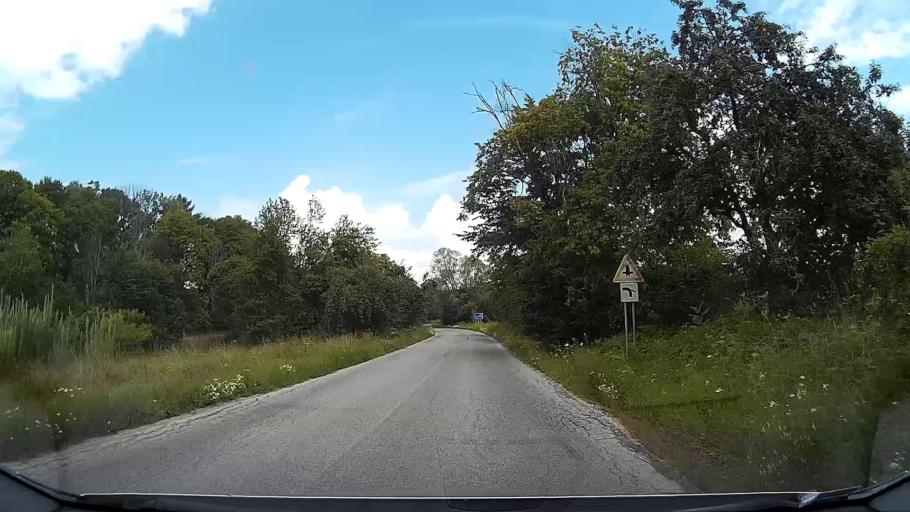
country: SK
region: Presovsky
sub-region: Okres Poprad
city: Poprad
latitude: 48.9896
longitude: 20.3860
